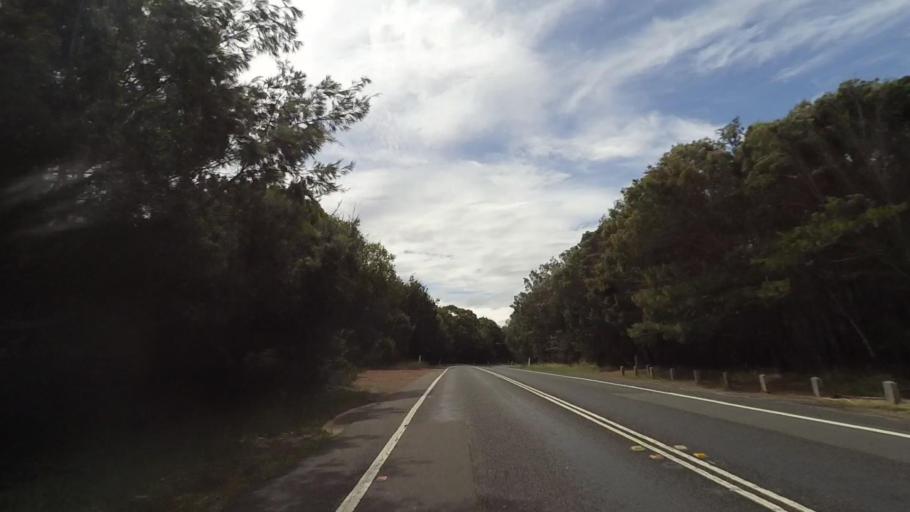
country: AU
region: New South Wales
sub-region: Sutherland Shire
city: Loftus
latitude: -34.0554
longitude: 151.0485
